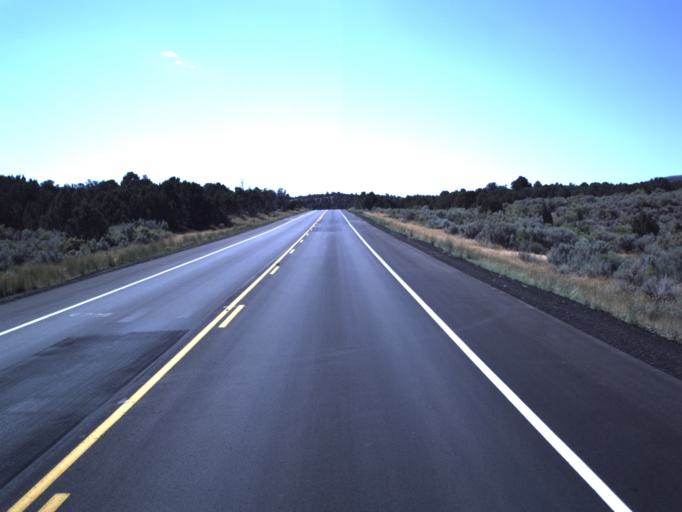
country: US
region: Utah
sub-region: Utah County
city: Eagle Mountain
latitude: 40.0082
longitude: -112.2762
